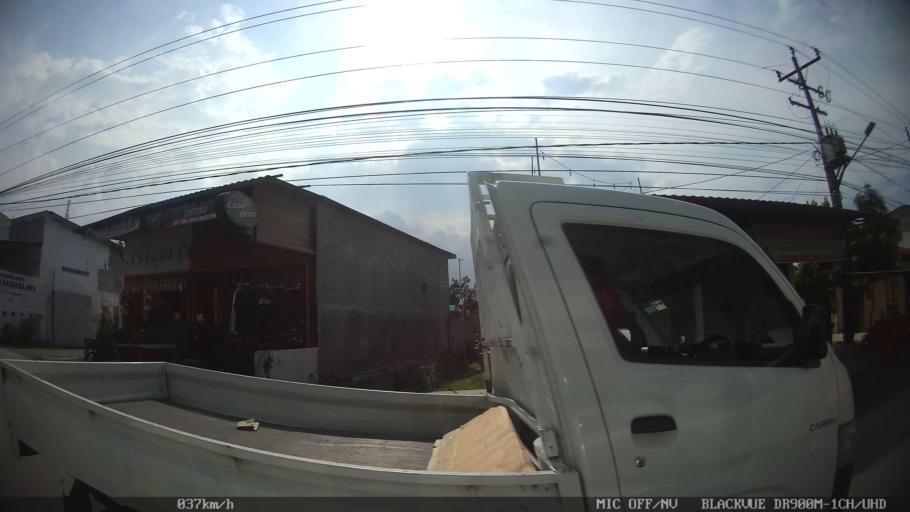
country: ID
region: North Sumatra
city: Medan
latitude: 3.5877
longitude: 98.7569
